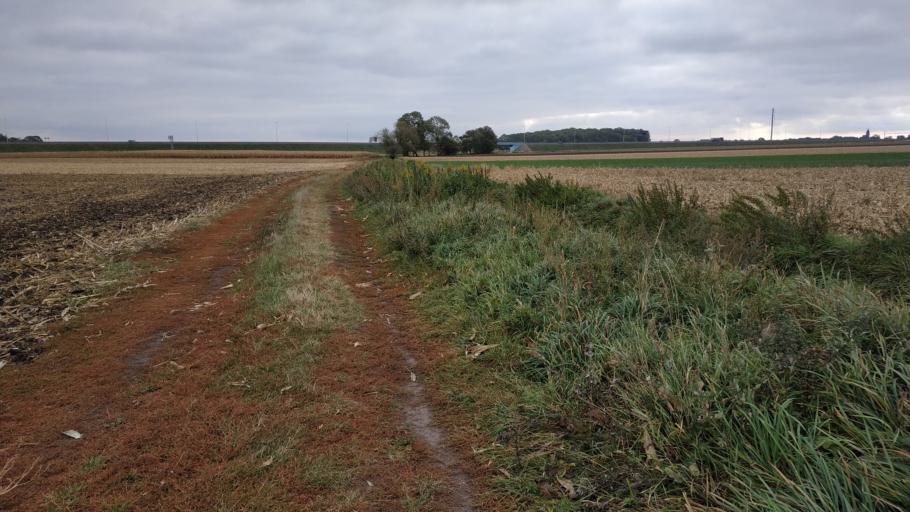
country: PL
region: Lower Silesian Voivodeship
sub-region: Powiat wroclawski
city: Tyniec Maly
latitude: 51.0255
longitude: 16.9351
